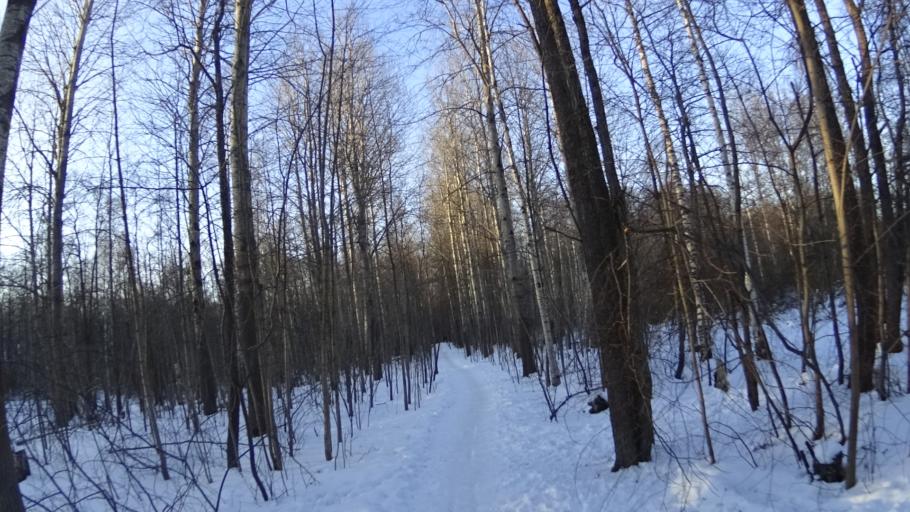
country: FI
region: Uusimaa
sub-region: Helsinki
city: Teekkarikylae
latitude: 60.2113
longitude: 24.8528
